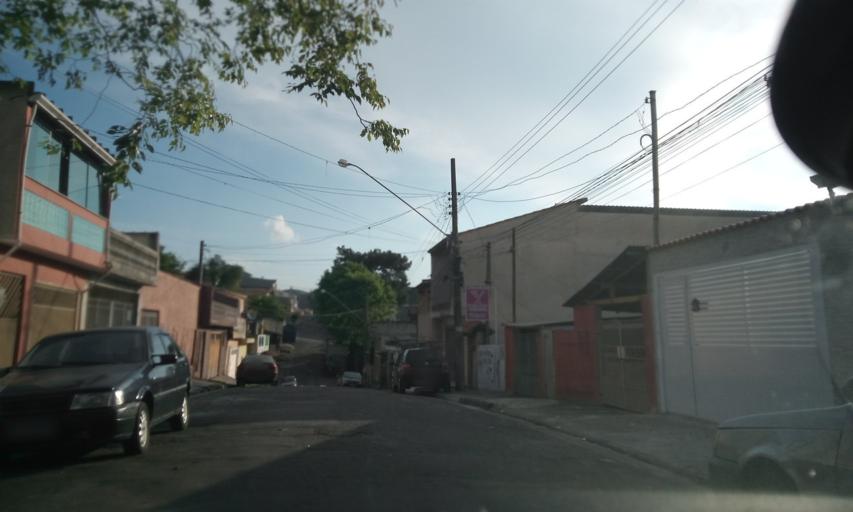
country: BR
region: Sao Paulo
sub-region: Santo Andre
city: Santo Andre
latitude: -23.7104
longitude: -46.5049
